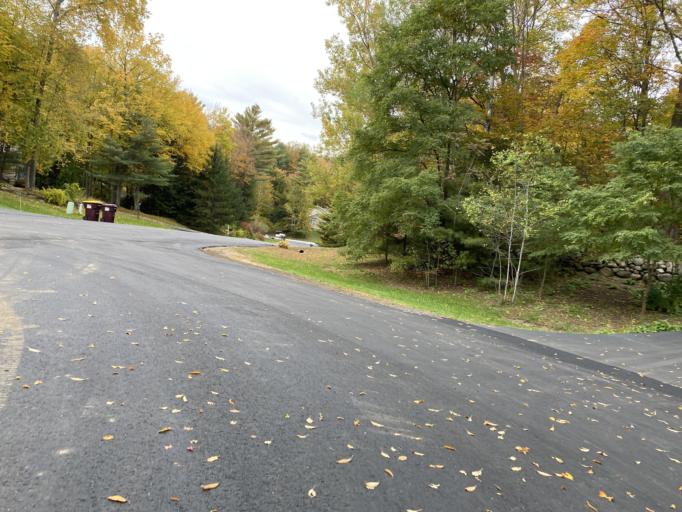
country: US
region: New York
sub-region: Saratoga County
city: Milton
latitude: 43.0935
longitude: -73.9050
